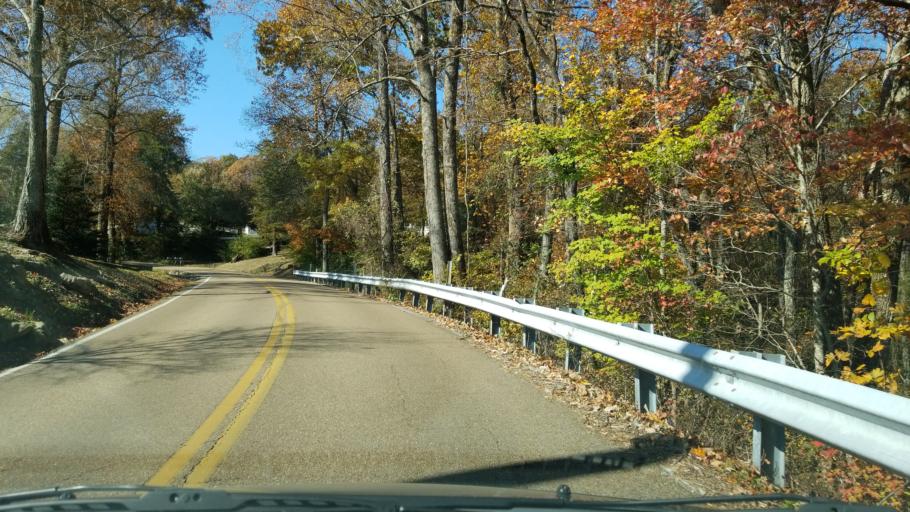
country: US
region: Tennessee
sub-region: Hamilton County
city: Soddy-Daisy
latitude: 35.2547
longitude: -85.1978
